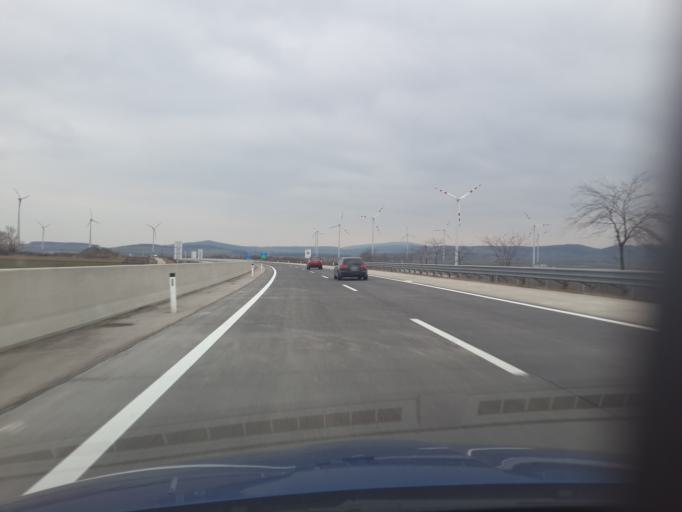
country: AT
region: Burgenland
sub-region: Politischer Bezirk Neusiedl am See
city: Kittsee
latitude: 48.0808
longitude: 17.0453
